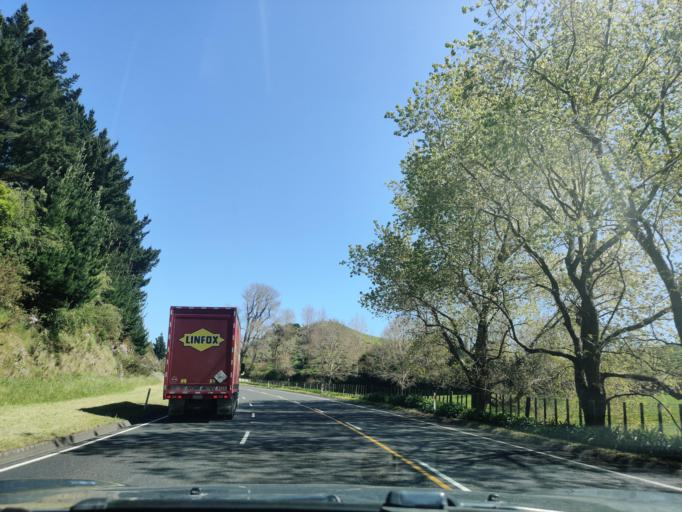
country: NZ
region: Manawatu-Wanganui
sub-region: Wanganui District
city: Wanganui
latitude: -39.8262
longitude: 174.8808
